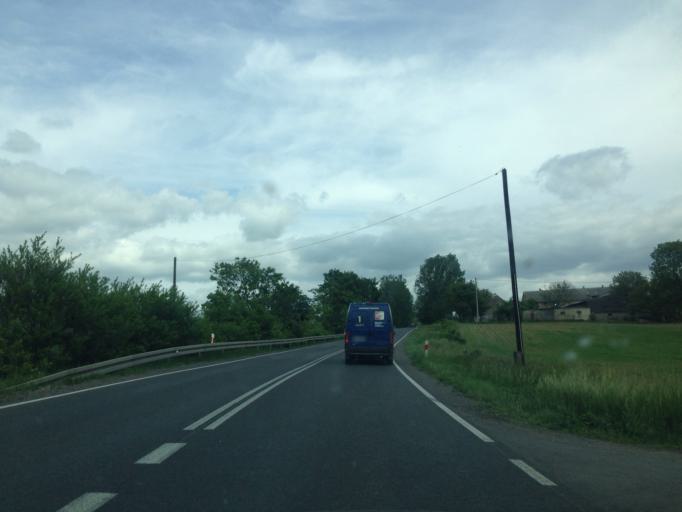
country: PL
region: Kujawsko-Pomorskie
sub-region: Powiat brodnicki
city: Bobrowo
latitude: 53.2495
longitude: 19.3059
